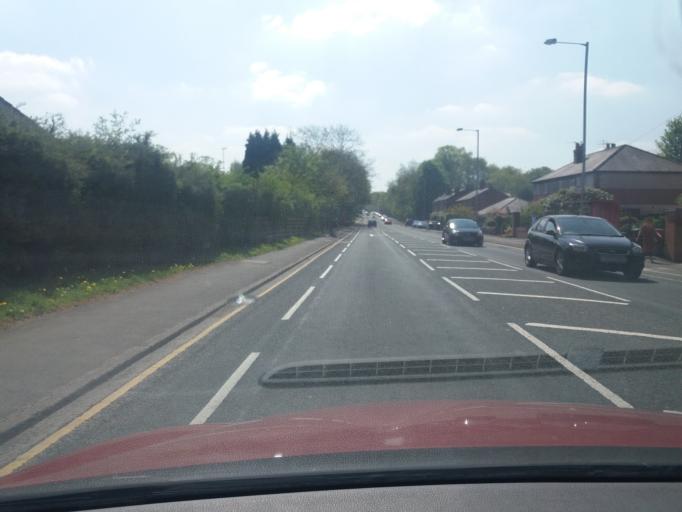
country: GB
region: England
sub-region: Lancashire
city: Clayton-le-Woods
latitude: 53.6923
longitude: -2.6387
